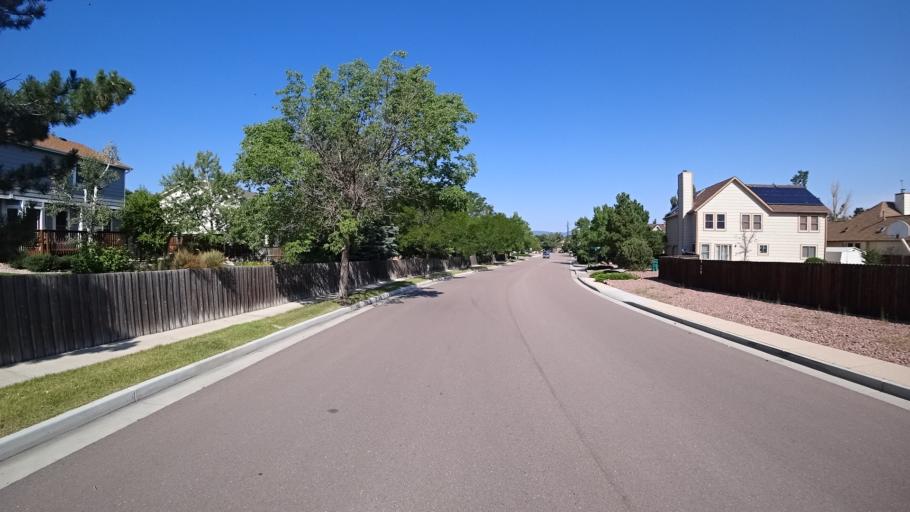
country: US
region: Colorado
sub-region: El Paso County
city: Air Force Academy
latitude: 38.9552
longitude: -104.7806
